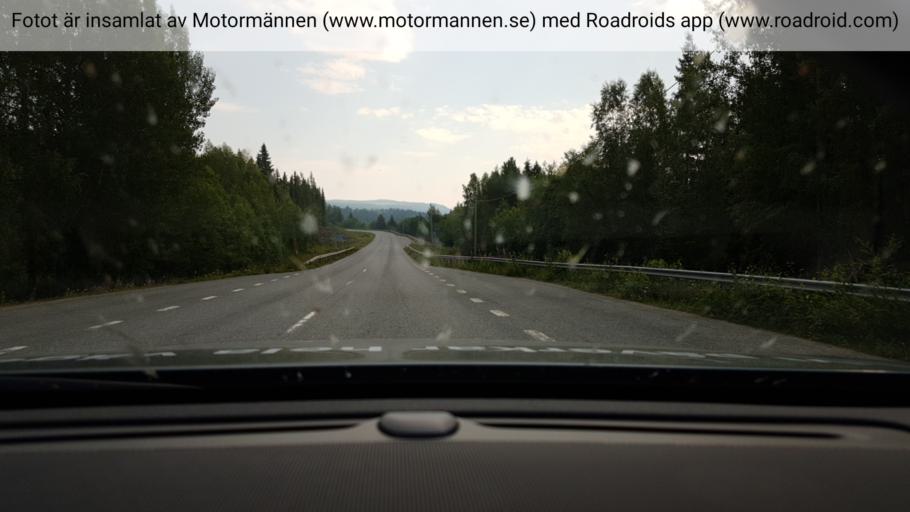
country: SE
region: Vaesterbotten
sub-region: Vilhelmina Kommun
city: Sjoberg
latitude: 65.4732
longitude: 16.0417
